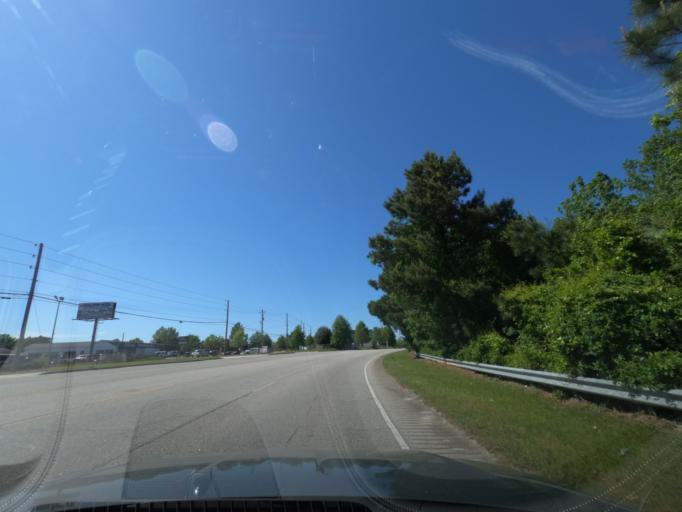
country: US
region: Georgia
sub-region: Columbia County
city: Evans
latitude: 33.4713
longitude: -82.1254
